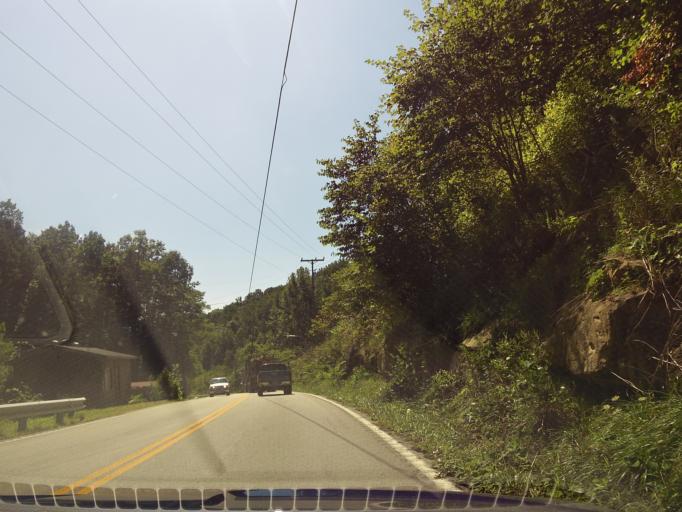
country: US
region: Kentucky
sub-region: Leslie County
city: Hyden
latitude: 37.1367
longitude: -83.4695
